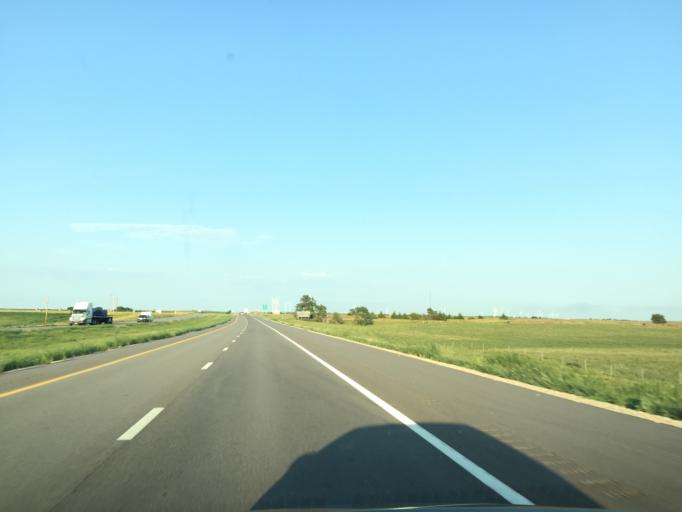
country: US
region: Kansas
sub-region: Ellsworth County
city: Ellsworth
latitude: 38.8486
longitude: -98.4890
